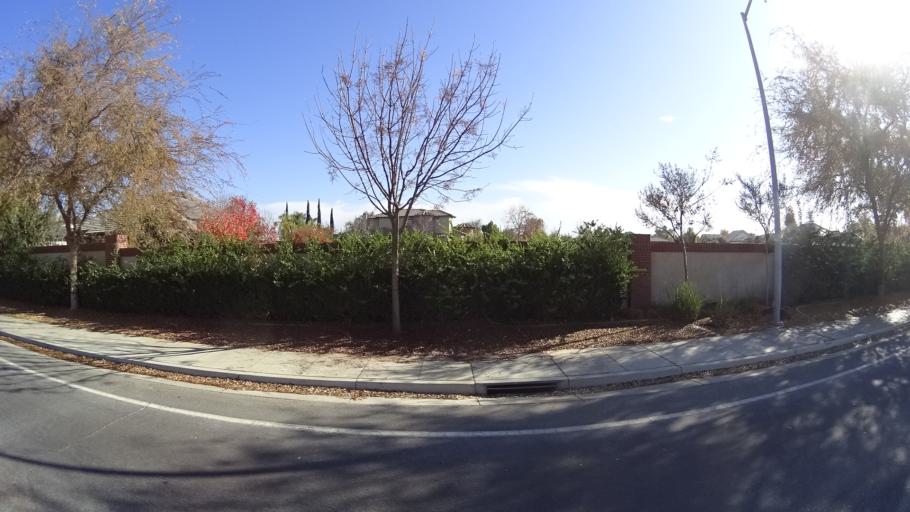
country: US
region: California
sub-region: Kern County
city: Rosedale
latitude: 35.3350
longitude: -119.1455
